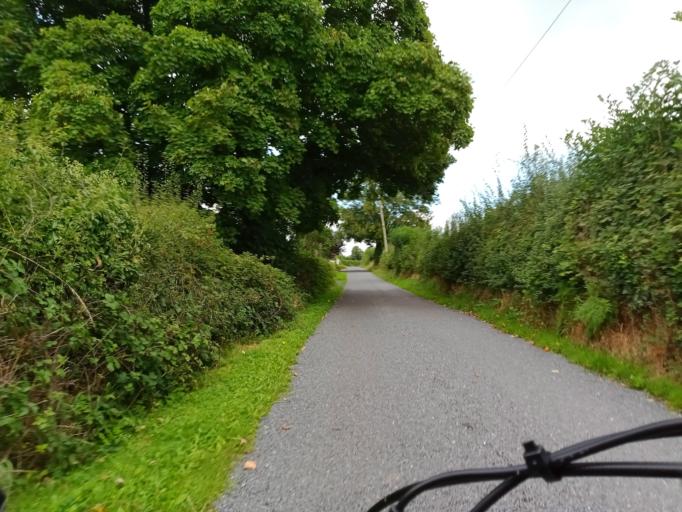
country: IE
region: Leinster
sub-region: Kilkenny
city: Callan
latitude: 52.5314
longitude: -7.2876
